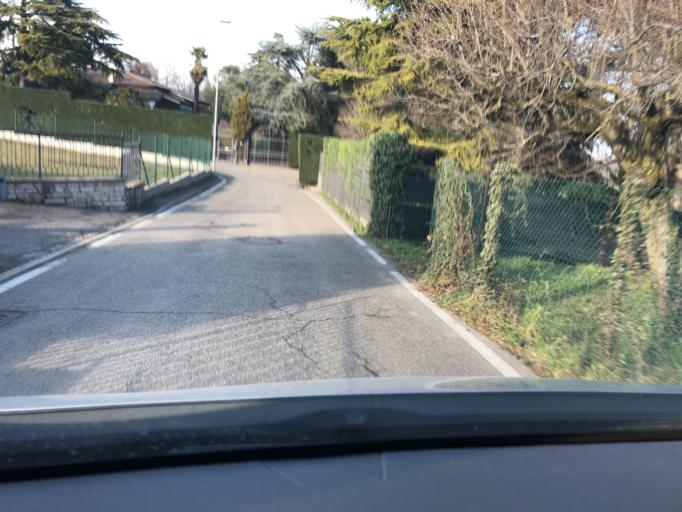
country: IT
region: Veneto
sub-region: Provincia di Verona
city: Sommacampagna
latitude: 45.4145
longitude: 10.8478
